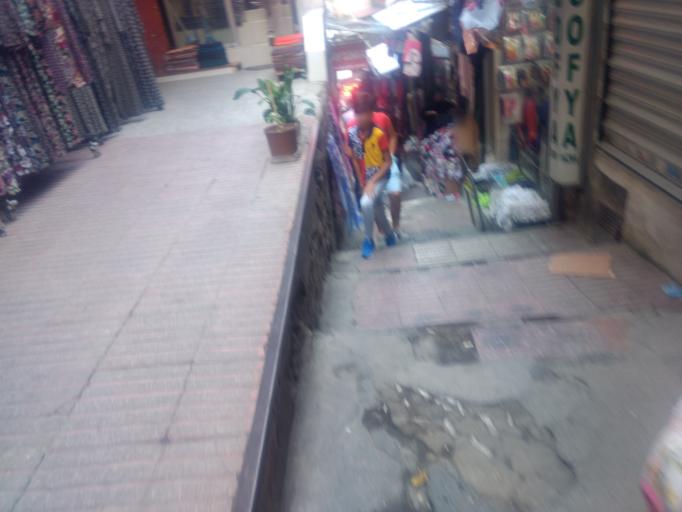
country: TR
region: Istanbul
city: Eminoenue
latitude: 41.0116
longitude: 28.9700
